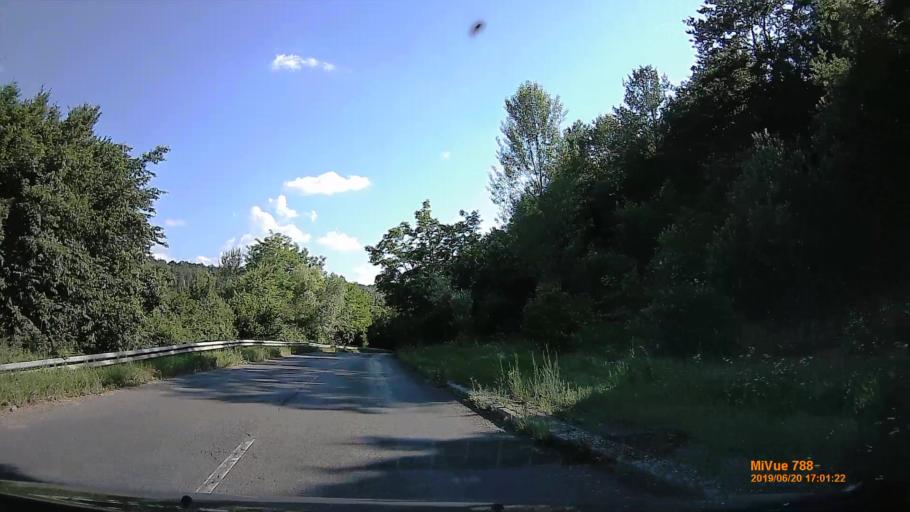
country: HU
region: Baranya
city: Buekkoesd
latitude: 46.1256
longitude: 18.0295
